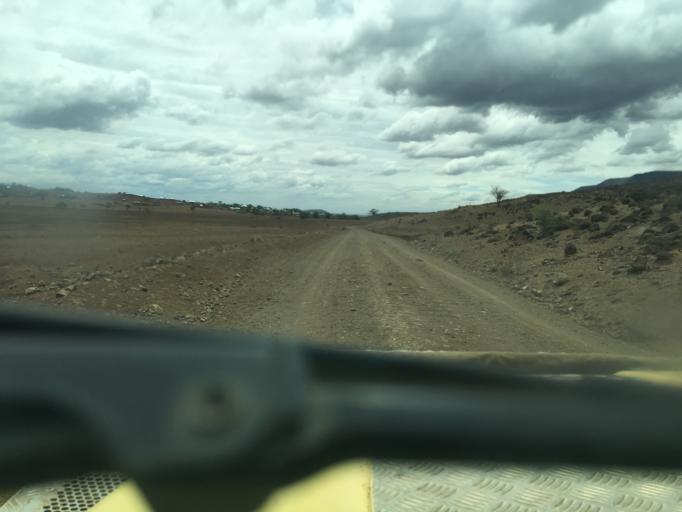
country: TZ
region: Arusha
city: Mto wa Mbu
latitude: -3.1932
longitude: 35.9459
